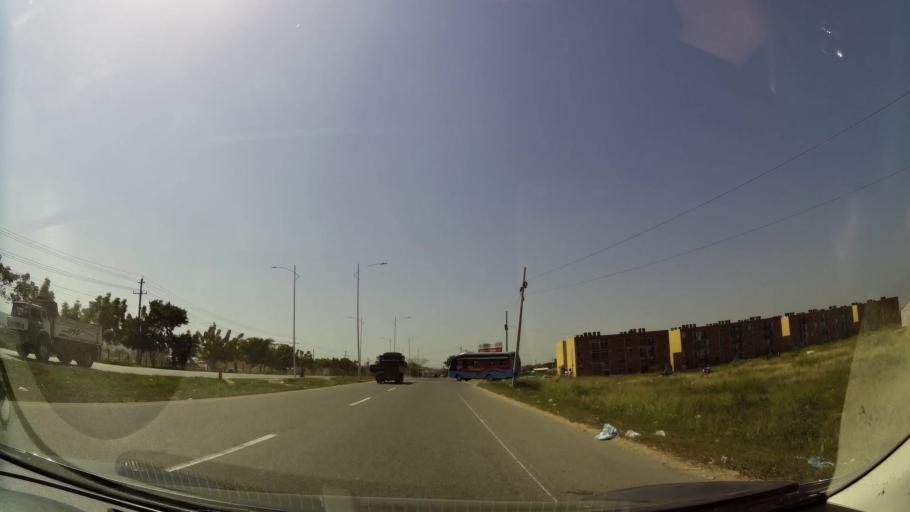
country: CO
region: Bolivar
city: Cartagena
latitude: 10.3919
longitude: -75.4486
